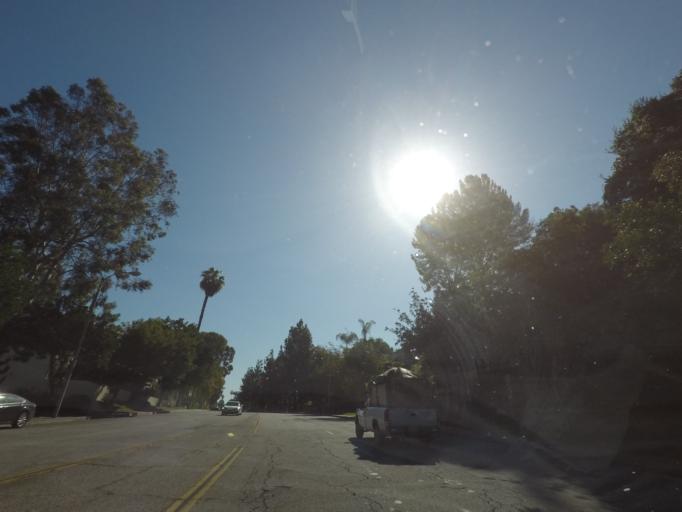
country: US
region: California
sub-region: Los Angeles County
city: South Pasadena
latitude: 34.1113
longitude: -118.1680
